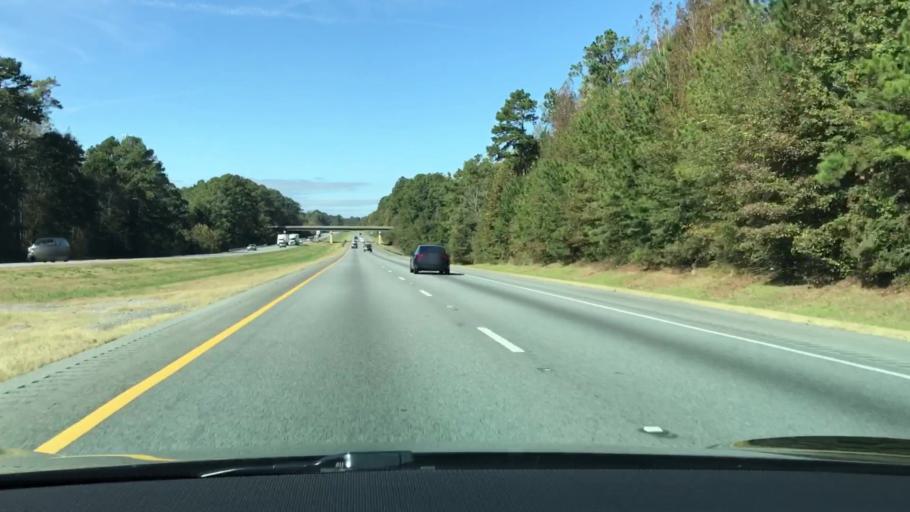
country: US
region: Georgia
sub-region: Morgan County
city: Madison
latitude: 33.5716
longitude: -83.5213
